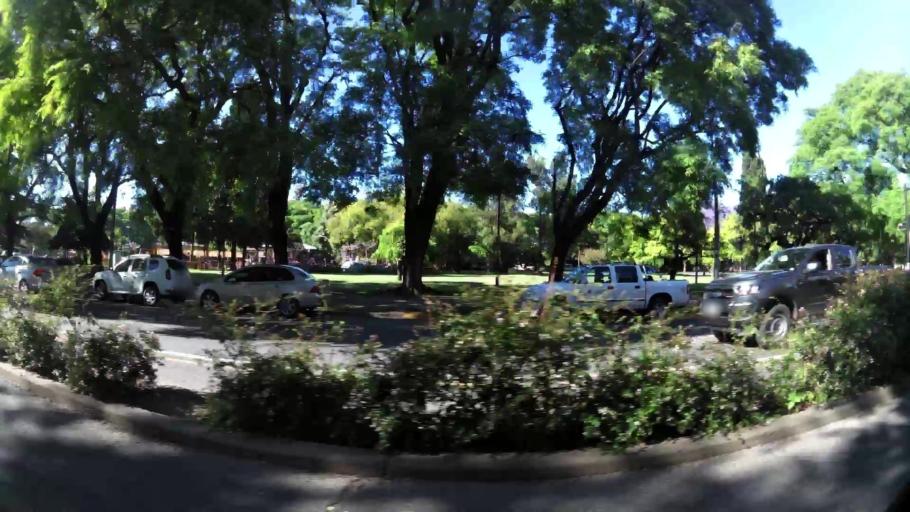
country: AR
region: Santa Fe
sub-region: Departamento de Rosario
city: Rosario
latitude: -32.9536
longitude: -60.6614
